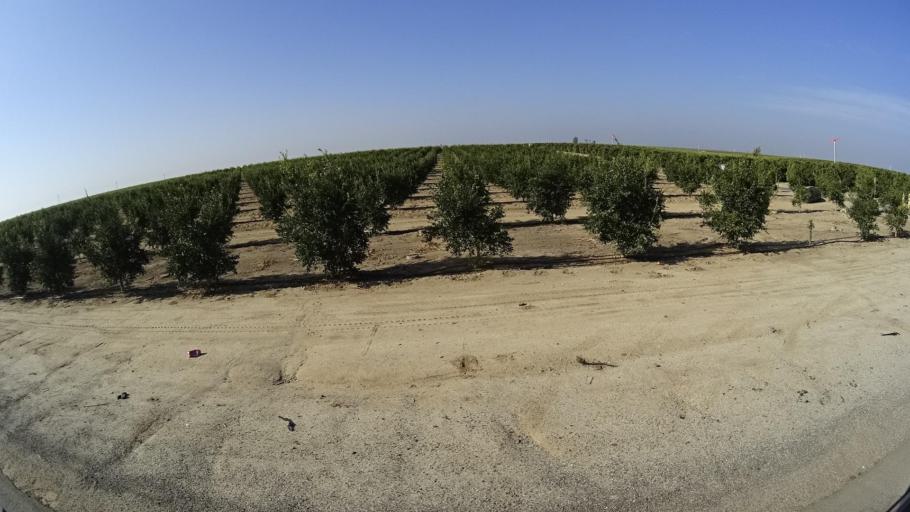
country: US
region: California
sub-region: Kern County
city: McFarland
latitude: 35.6056
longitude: -119.1688
